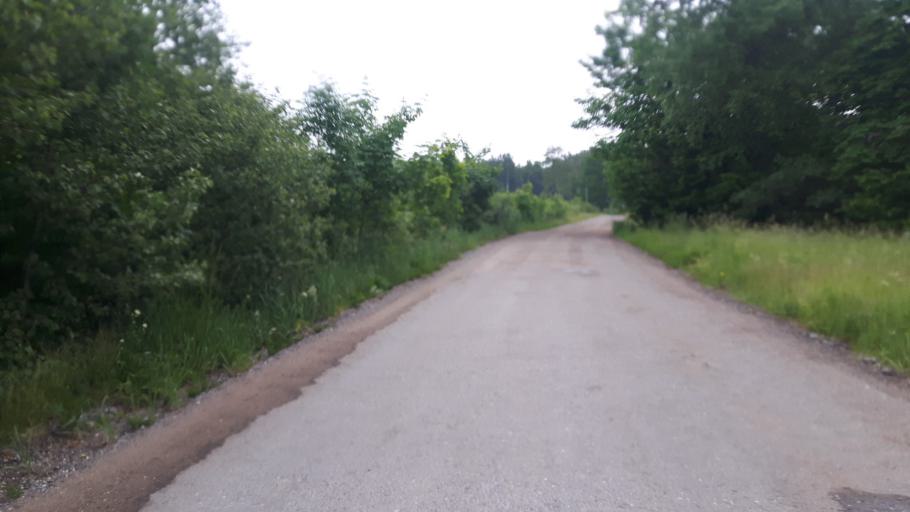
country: LV
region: Salacgrivas
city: Salacgriva
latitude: 57.6880
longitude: 24.3727
